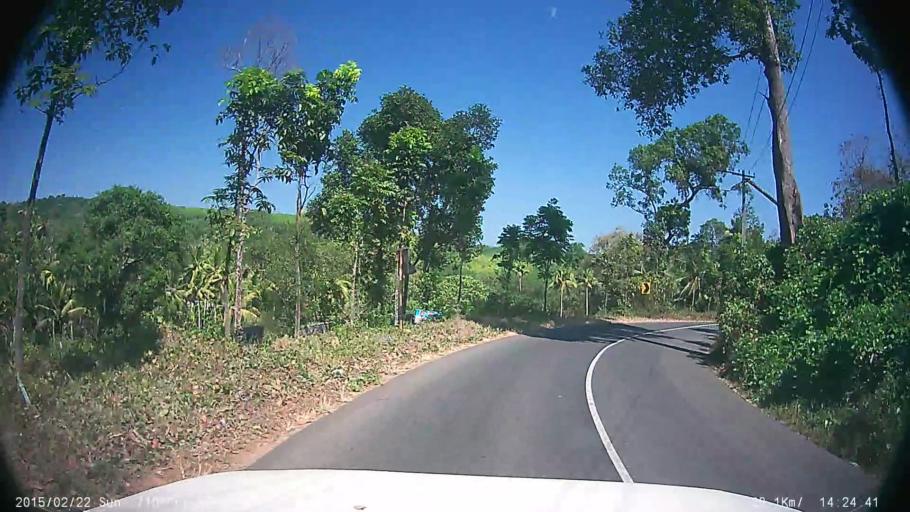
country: IN
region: Kerala
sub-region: Kottayam
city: Erattupetta
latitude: 9.5709
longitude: 76.7160
